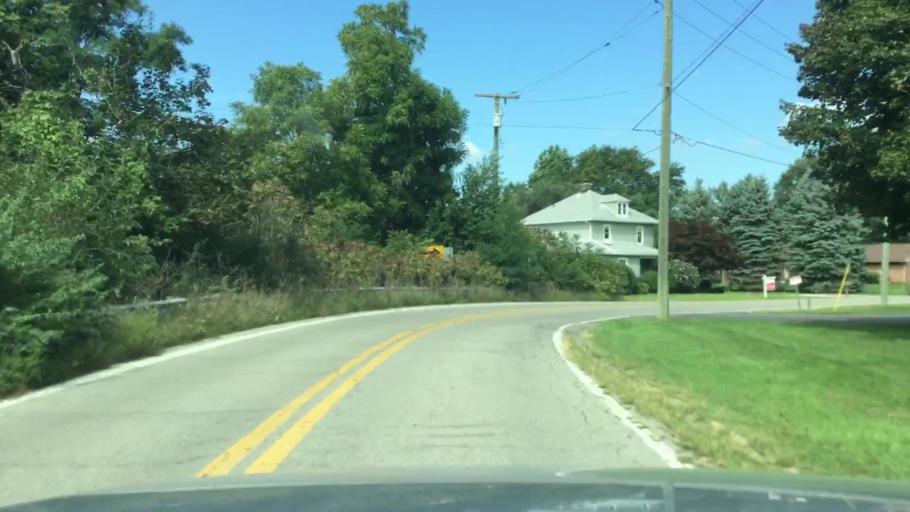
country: US
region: Michigan
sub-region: Wayne County
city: Belleville
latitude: 42.2154
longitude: -83.4940
